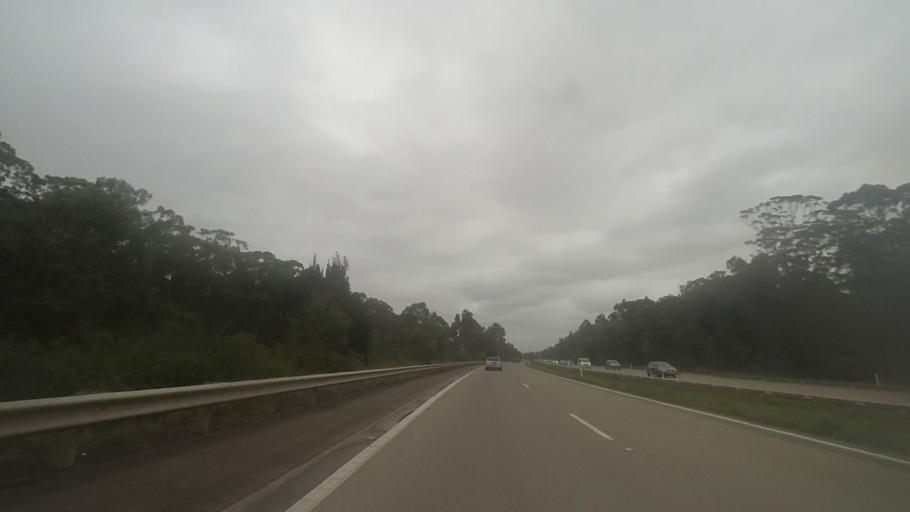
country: AU
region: New South Wales
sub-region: Port Stephens Shire
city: Medowie
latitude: -32.6961
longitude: 151.8073
